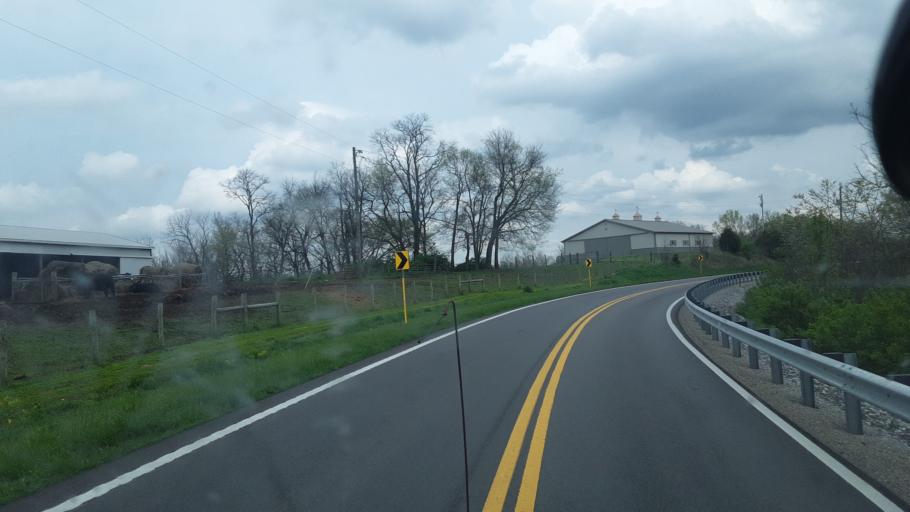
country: US
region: Kentucky
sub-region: Grant County
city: Dry Ridge
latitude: 38.6711
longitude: -84.6376
